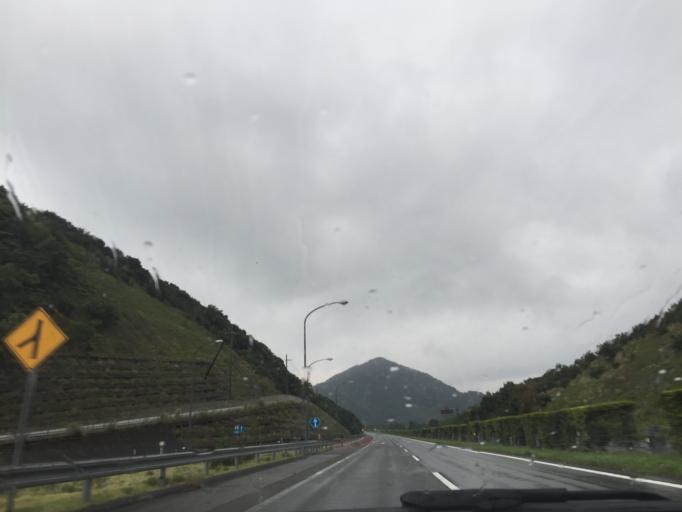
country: JP
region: Tokushima
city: Narutocho-mitsuishi
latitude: 34.2200
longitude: 134.6262
